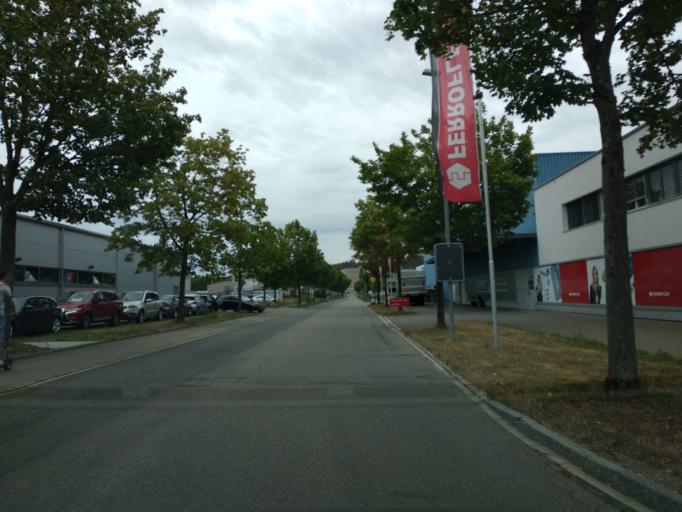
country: CH
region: Schaffhausen
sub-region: Bezirk Reiat
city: Stetten
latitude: 47.7166
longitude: 8.6571
